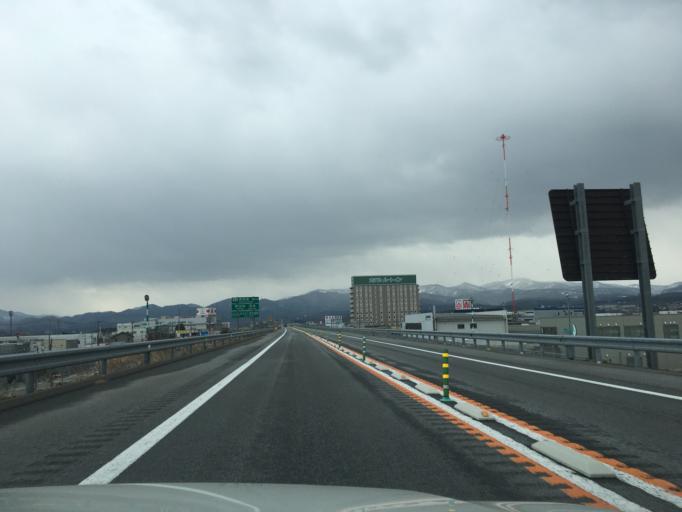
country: JP
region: Aomori
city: Aomori Shi
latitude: 40.7953
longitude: 140.7541
